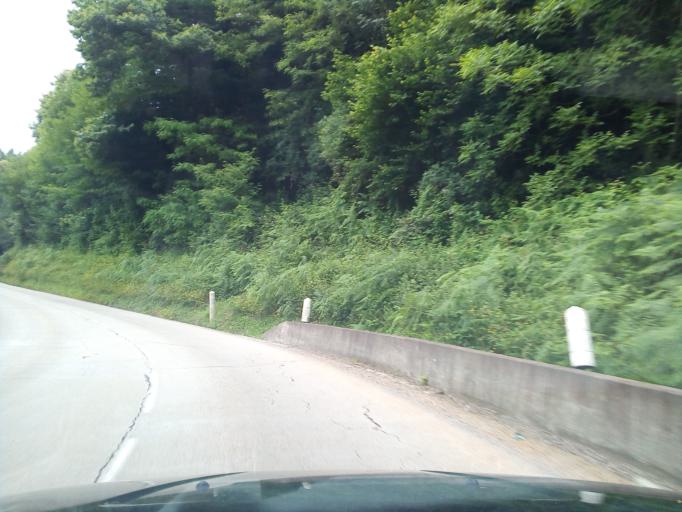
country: FR
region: Rhone-Alpes
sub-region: Departement de l'Isere
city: Vaulnaveys-le-Haut
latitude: 45.1392
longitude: 5.8332
